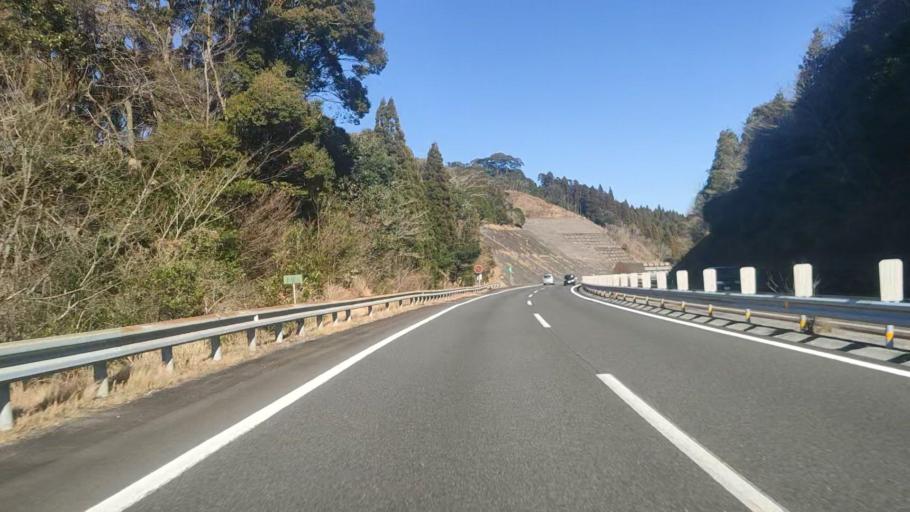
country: JP
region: Miyazaki
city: Miyakonojo
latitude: 31.8196
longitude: 131.2174
